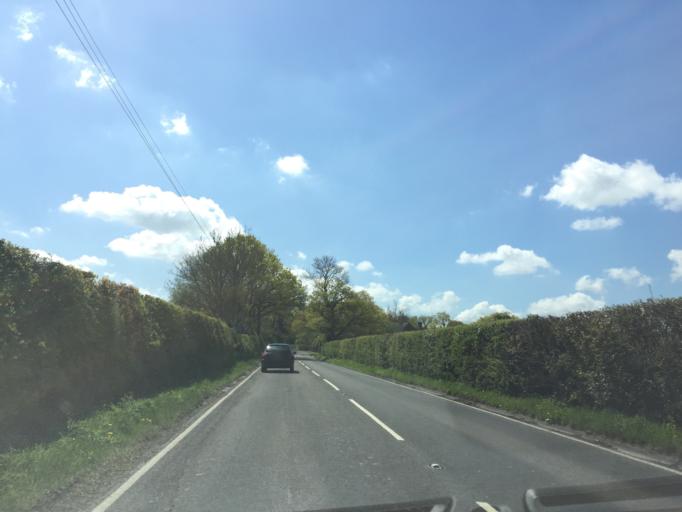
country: GB
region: England
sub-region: Kent
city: Edenbridge
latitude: 51.1369
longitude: 0.1074
